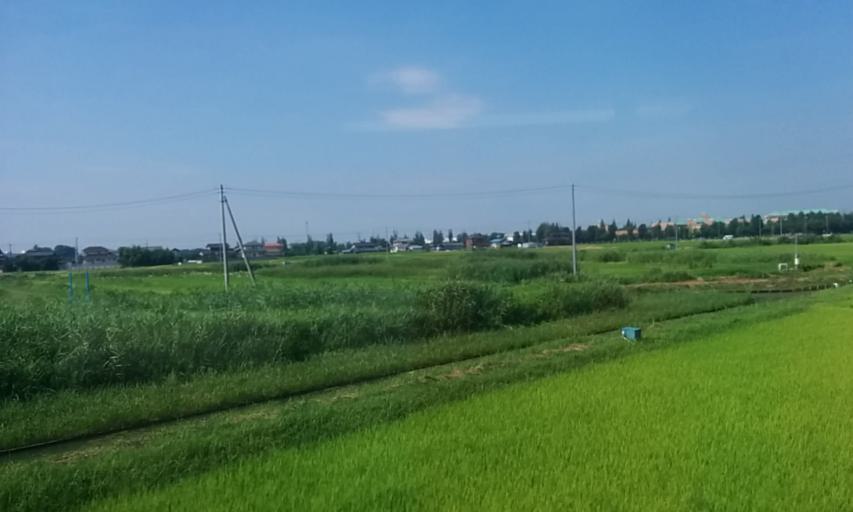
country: JP
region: Saitama
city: Kukichuo
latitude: 36.1038
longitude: 139.6499
